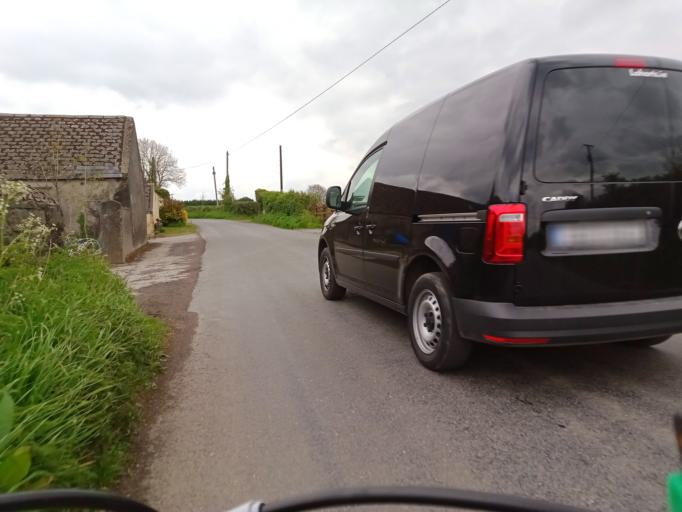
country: IE
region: Leinster
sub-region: Kilkenny
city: Kilkenny
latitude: 52.6183
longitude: -7.2589
